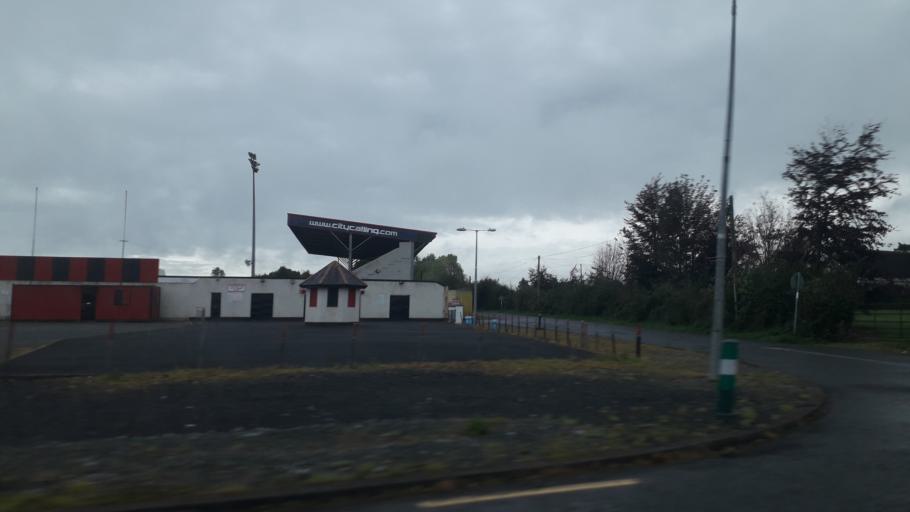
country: IE
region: Leinster
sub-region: An Longfort
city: Longford
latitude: 53.7255
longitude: -7.8536
